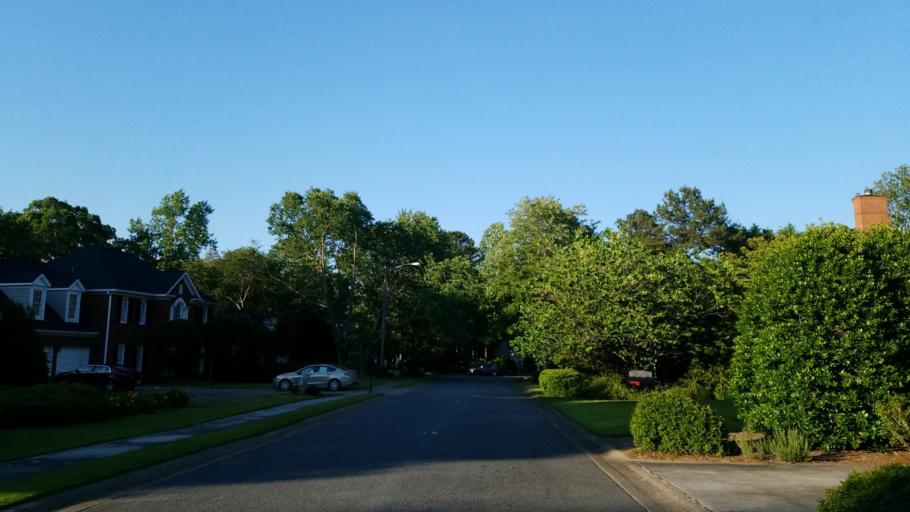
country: US
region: Georgia
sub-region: Cobb County
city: Vinings
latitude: 33.8724
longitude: -84.4872
